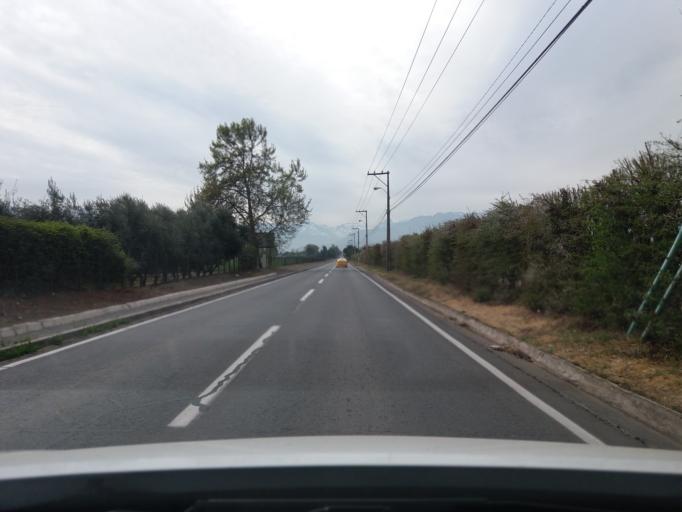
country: CL
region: Valparaiso
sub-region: Provincia de San Felipe
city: San Felipe
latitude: -32.8189
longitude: -70.6828
